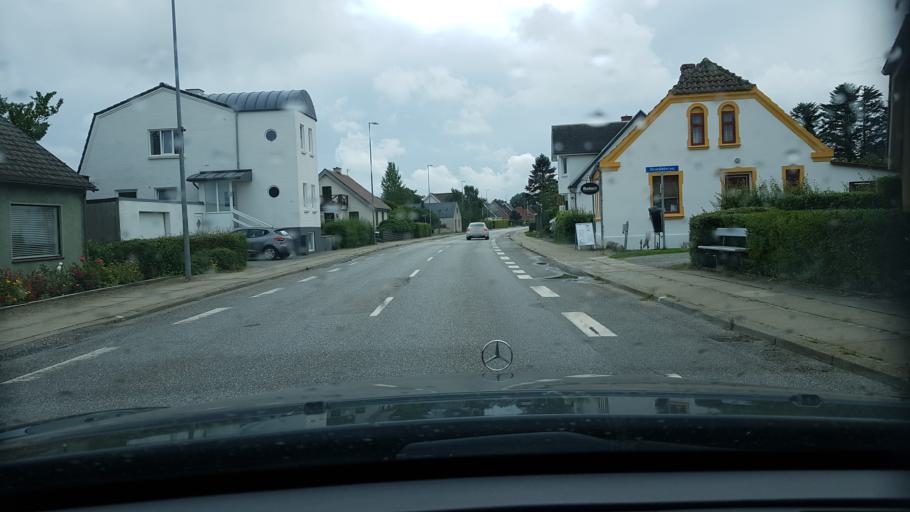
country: DK
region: North Denmark
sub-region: Mariagerfjord Kommune
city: Hadsund
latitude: 56.8012
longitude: 10.2729
